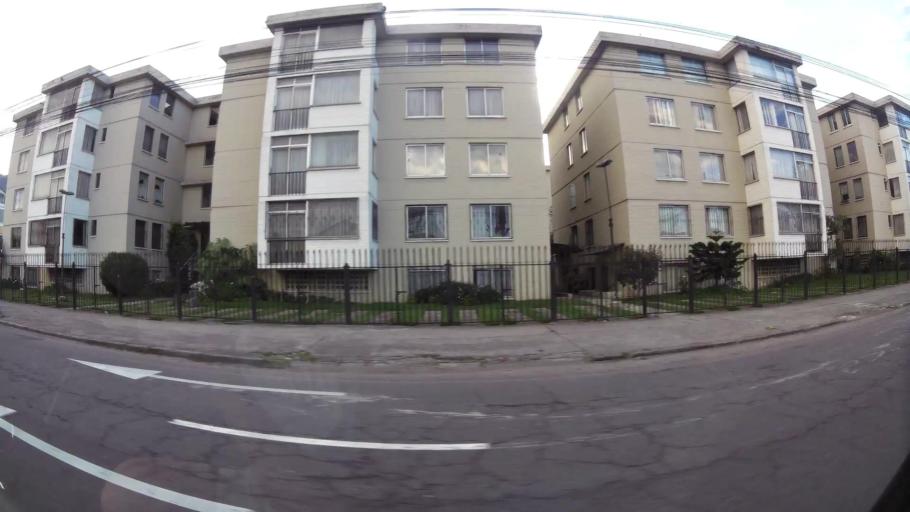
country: EC
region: Pichincha
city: Quito
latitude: -0.1646
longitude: -78.4842
